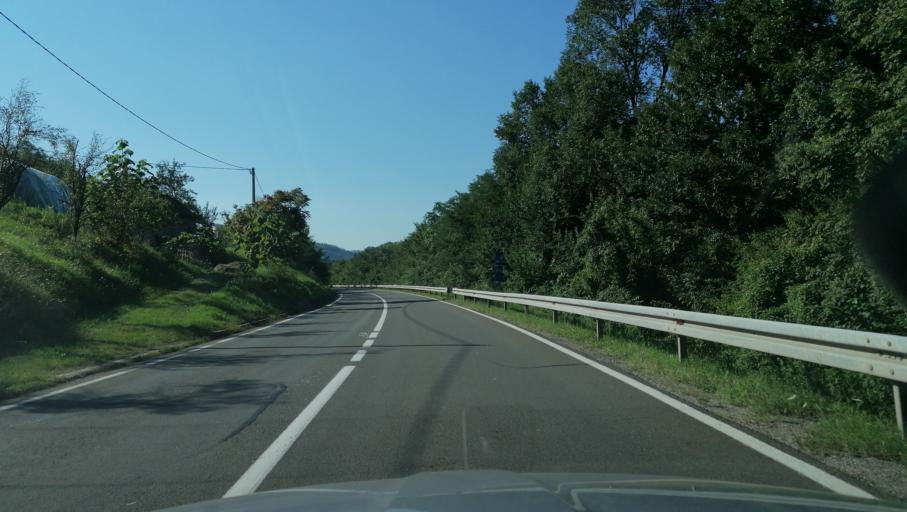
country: RS
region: Central Serbia
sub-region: Raski Okrug
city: Kraljevo
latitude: 43.6656
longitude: 20.5906
